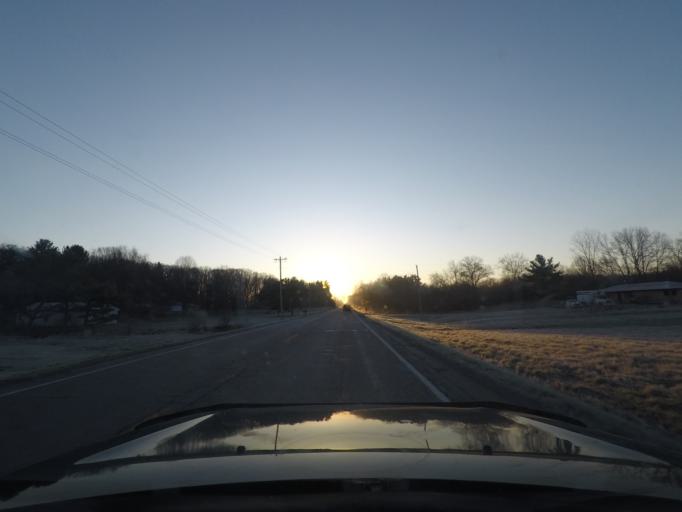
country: US
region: Indiana
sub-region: Marshall County
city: Plymouth
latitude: 41.4490
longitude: -86.3396
